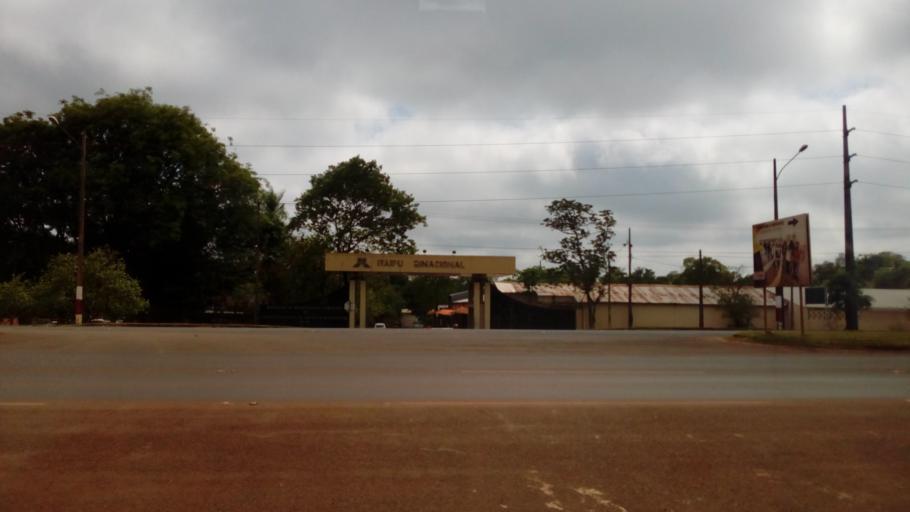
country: PY
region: Alto Parana
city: Ciudad del Este
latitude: -25.4413
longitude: -54.6343
